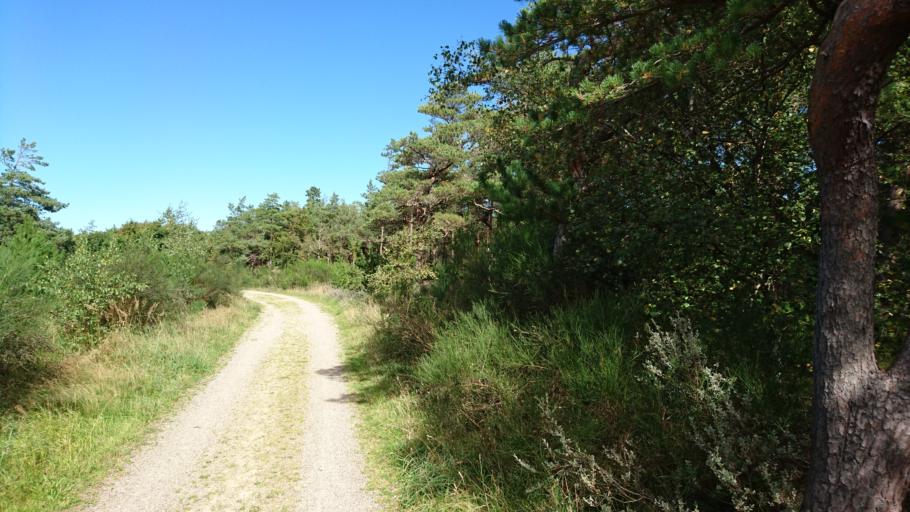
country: DK
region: North Denmark
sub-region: Frederikshavn Kommune
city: Skagen
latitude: 57.7188
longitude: 10.5299
